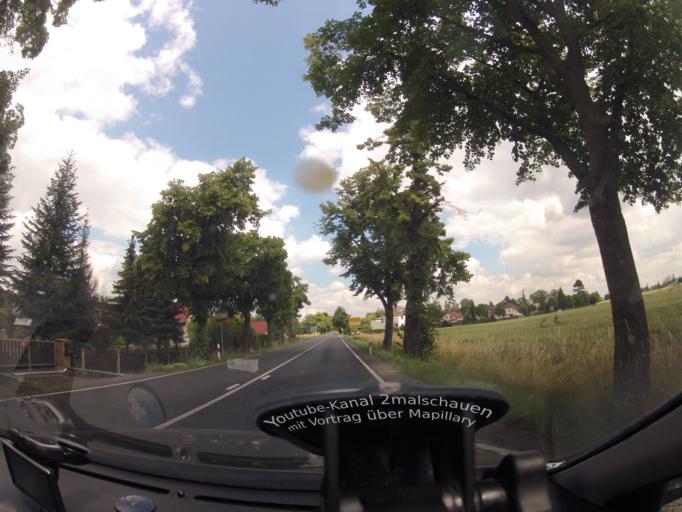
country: DE
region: Saxony
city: Jesewitz
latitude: 51.4152
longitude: 12.5471
